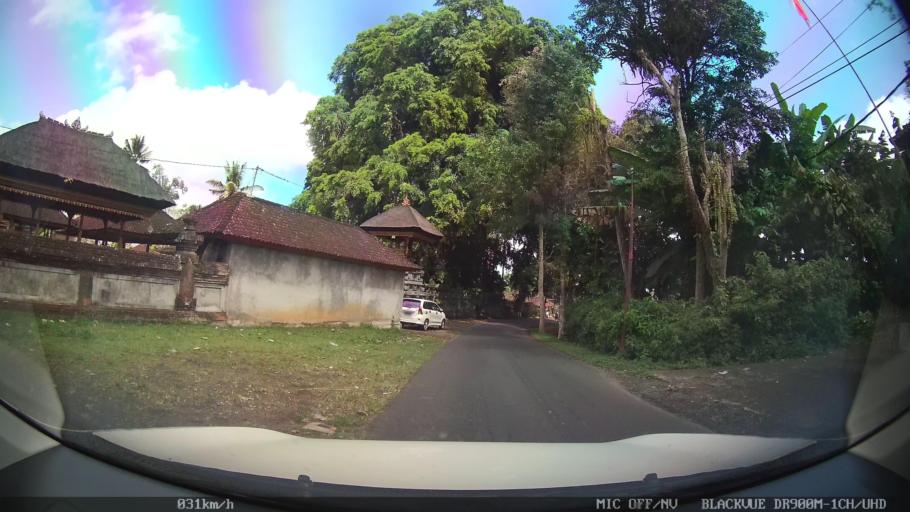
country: ID
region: Bali
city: Banjar Petak
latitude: -8.4559
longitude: 115.3202
